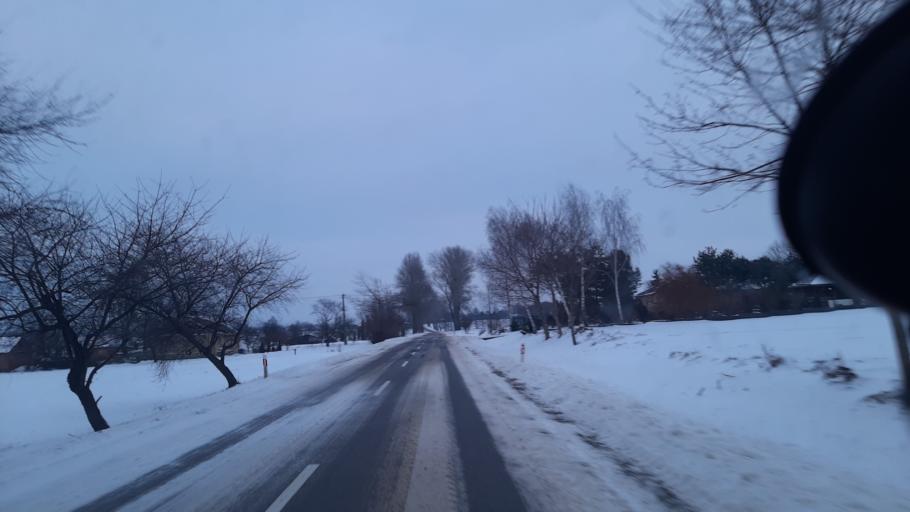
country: PL
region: Lublin Voivodeship
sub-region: Powiat lubelski
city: Garbow
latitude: 51.3458
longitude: 22.3864
